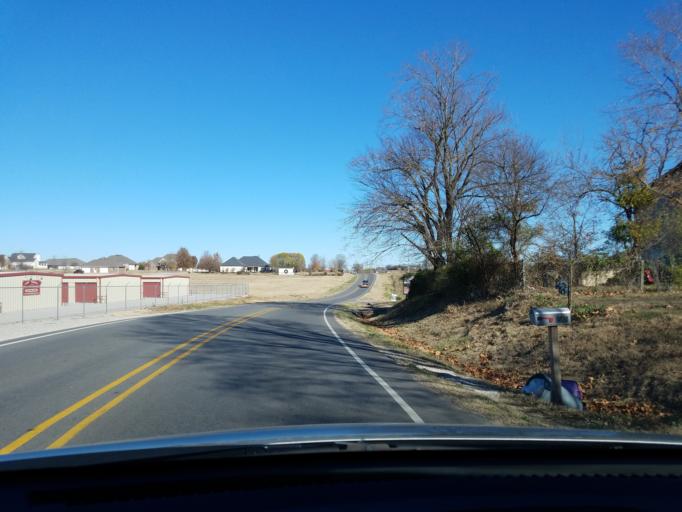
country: US
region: Arkansas
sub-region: Carroll County
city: Berryville
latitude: 36.3833
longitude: -93.5673
